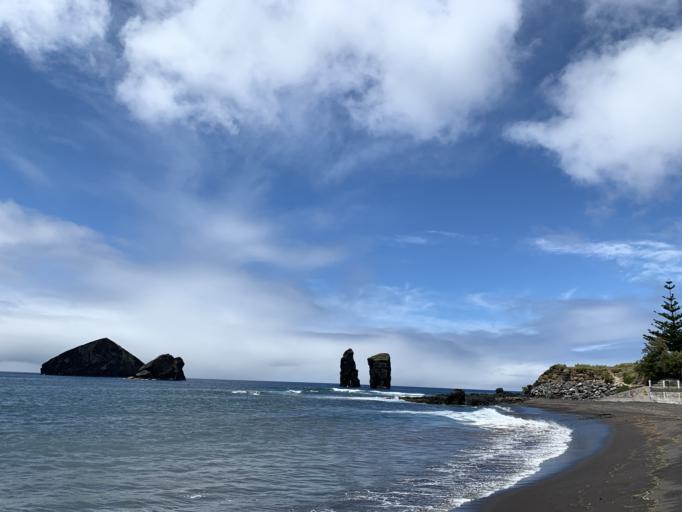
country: PT
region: Azores
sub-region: Ponta Delgada
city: Arrifes
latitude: 37.8880
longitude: -25.8239
